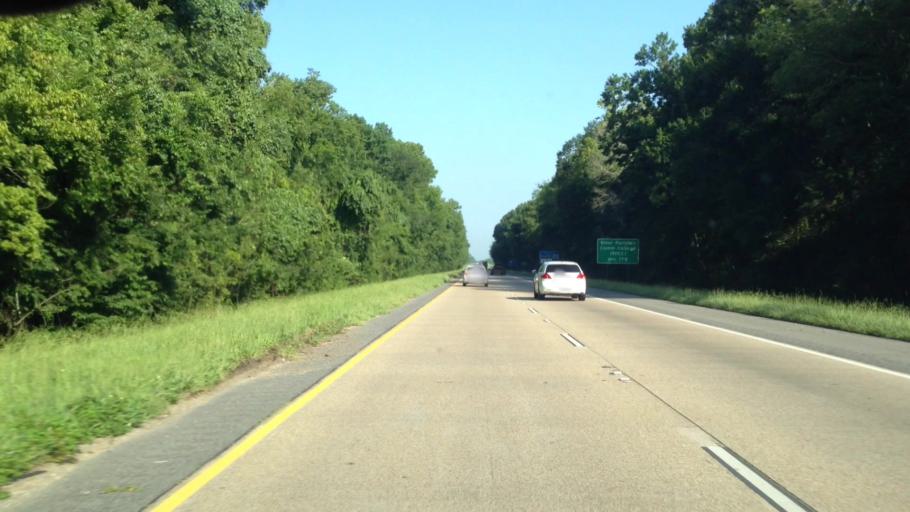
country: US
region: Louisiana
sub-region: Ascension Parish
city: Sorrento
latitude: 30.1870
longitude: -90.9084
